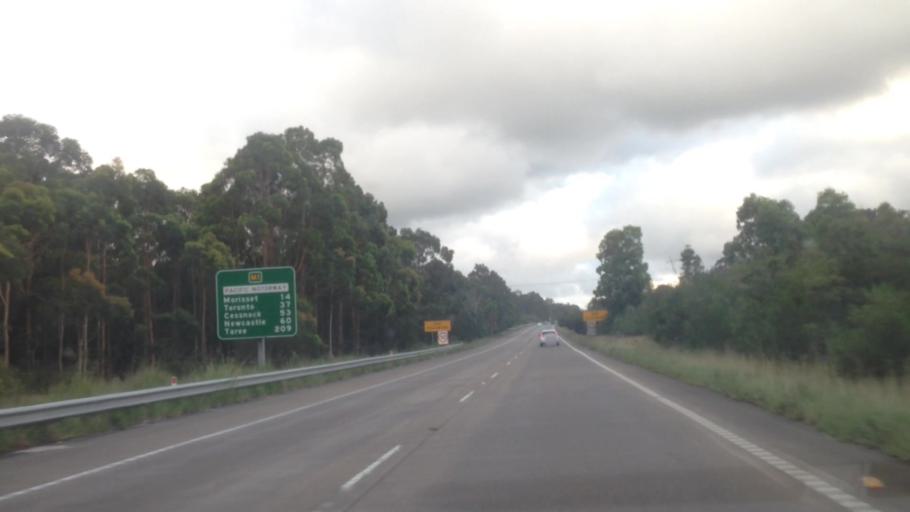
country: AU
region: New South Wales
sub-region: Wyong Shire
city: Jilliby
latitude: -33.2116
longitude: 151.4518
